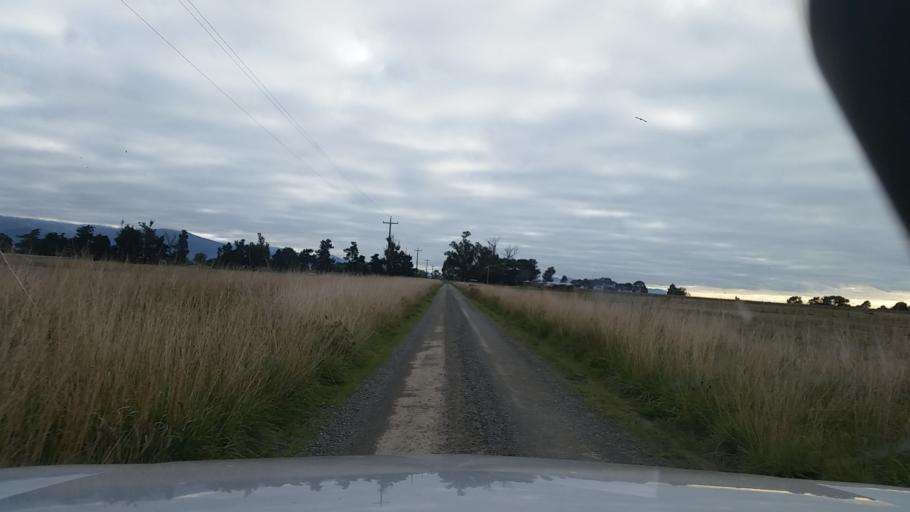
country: NZ
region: Marlborough
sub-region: Marlborough District
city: Blenheim
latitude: -41.5037
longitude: 174.0320
